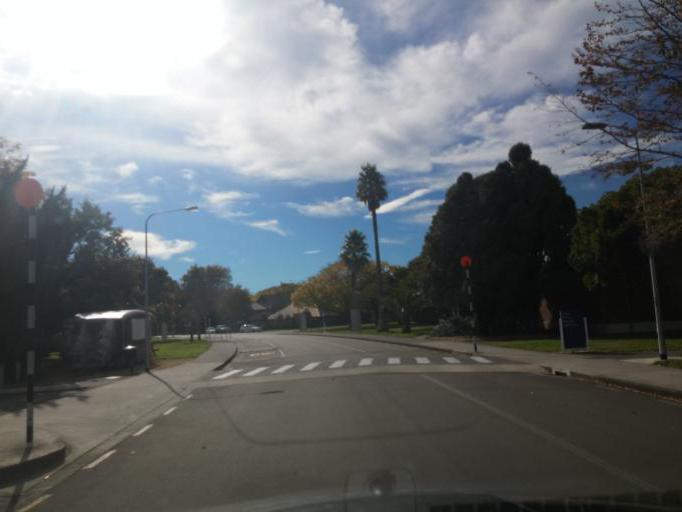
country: NZ
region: Manawatu-Wanganui
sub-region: Palmerston North City
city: Palmerston North
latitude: -40.3884
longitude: 175.6201
